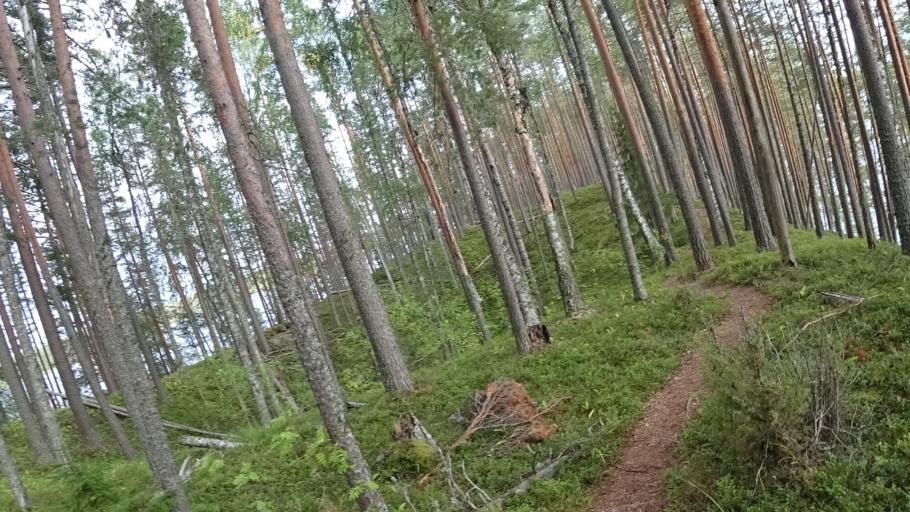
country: FI
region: North Karelia
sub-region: Joensuu
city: Ilomantsi
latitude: 62.5717
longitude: 31.1766
